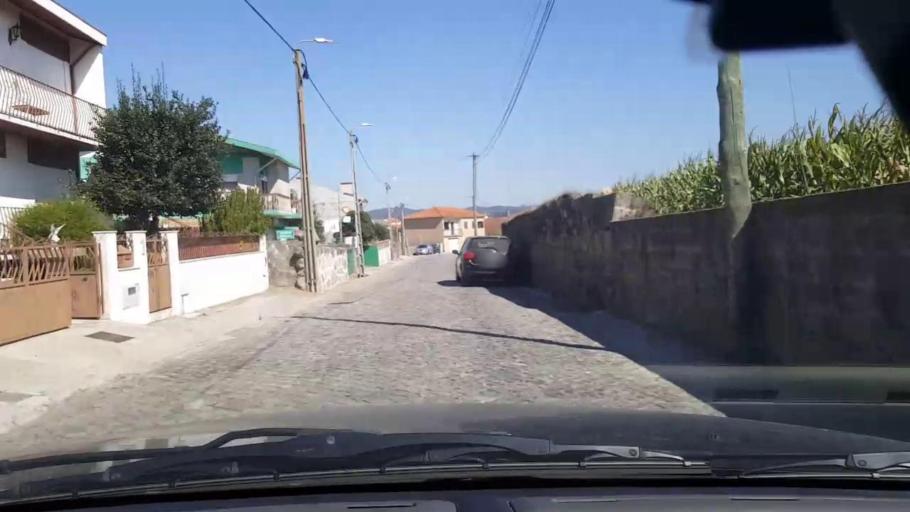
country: PT
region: Porto
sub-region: Matosinhos
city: Lavra
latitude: 41.2946
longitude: -8.6962
